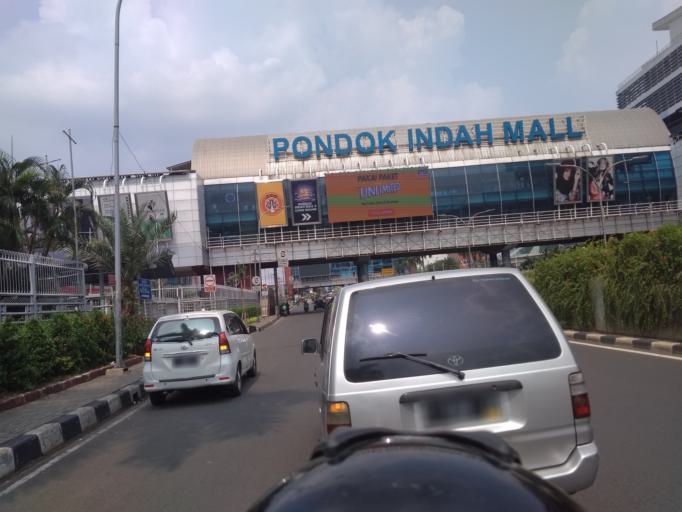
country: ID
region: Banten
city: South Tangerang
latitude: -6.2643
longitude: 106.7837
